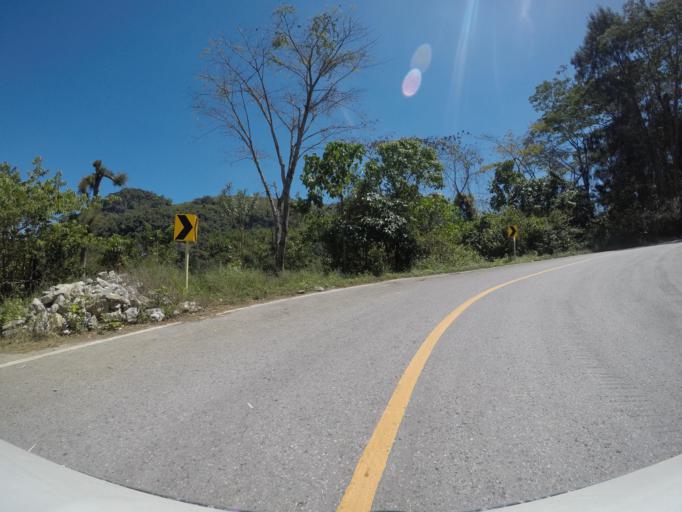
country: TL
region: Manatuto
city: Manatuto
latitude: -8.7705
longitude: 125.9645
